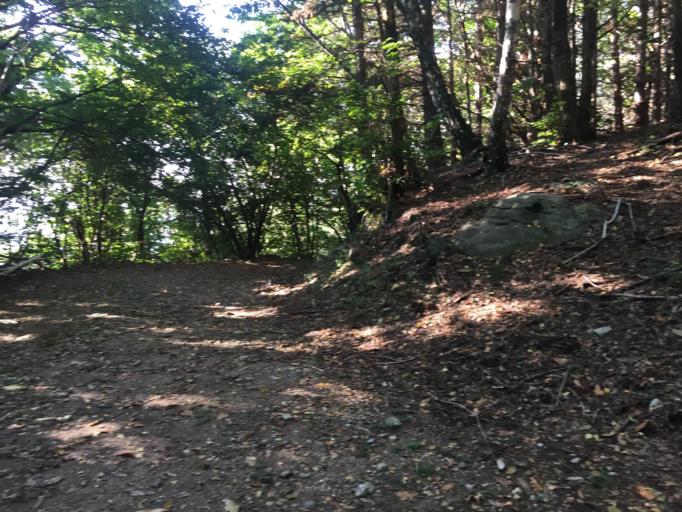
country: IT
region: Piedmont
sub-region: Provincia Verbano-Cusio-Ossola
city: Bee
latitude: 45.9695
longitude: 8.5769
